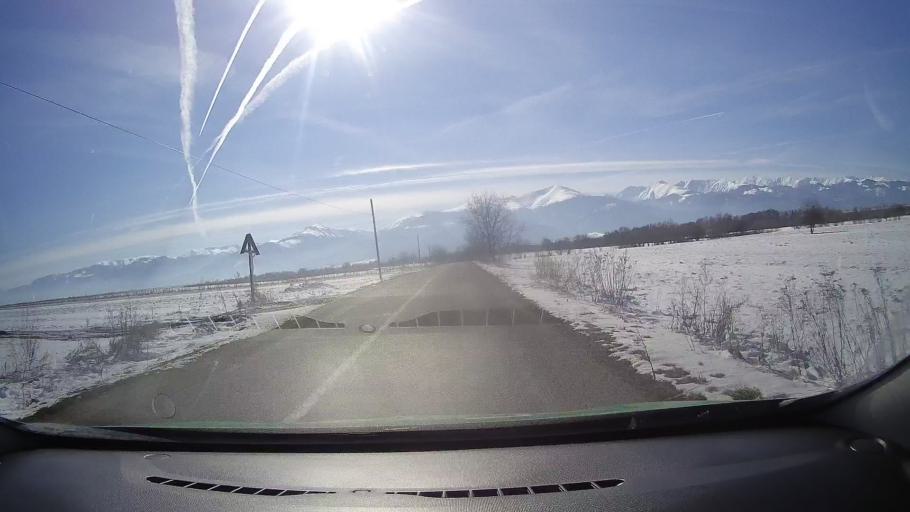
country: RO
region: Brasov
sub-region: Comuna Lisa
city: Lisa
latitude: 45.7433
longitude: 24.8434
